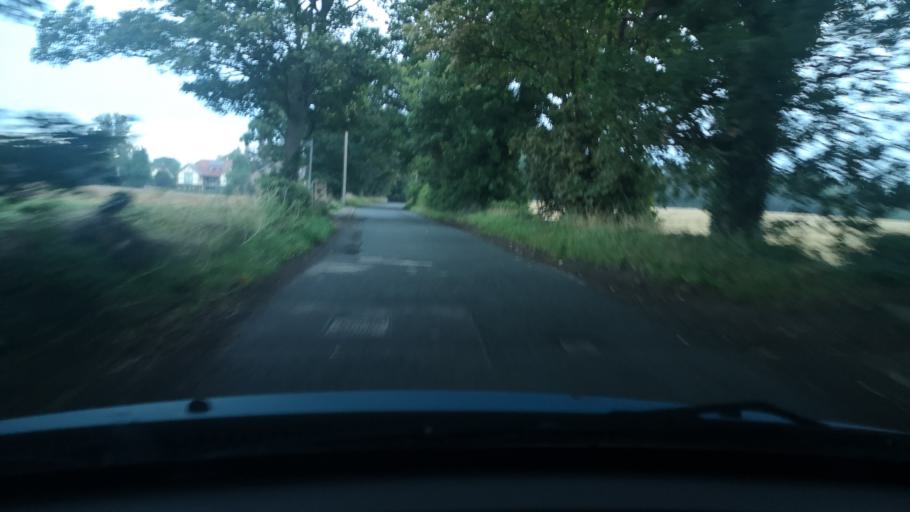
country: GB
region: England
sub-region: City and Borough of Wakefield
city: Low Ackworth
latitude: 53.6552
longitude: -1.3267
